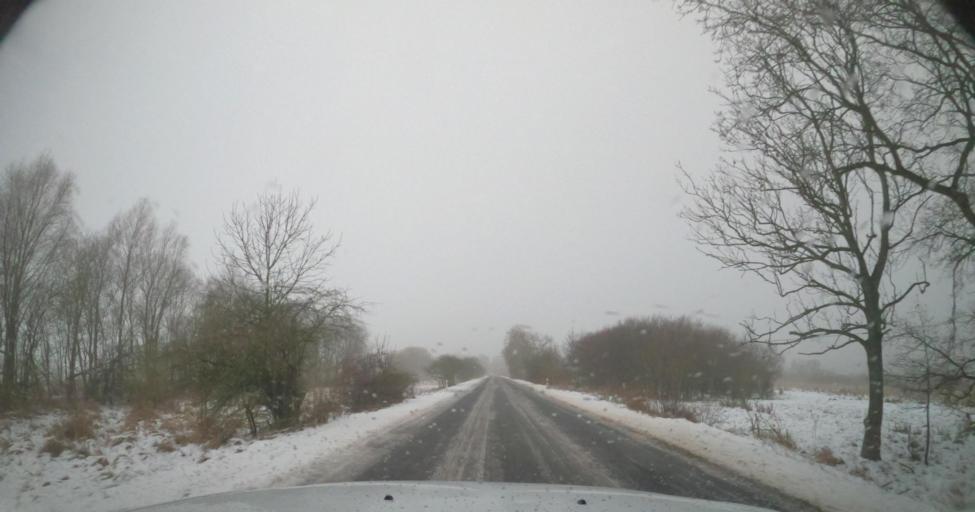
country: PL
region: West Pomeranian Voivodeship
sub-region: Powiat goleniowski
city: Stepnica
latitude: 53.5733
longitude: 14.7000
